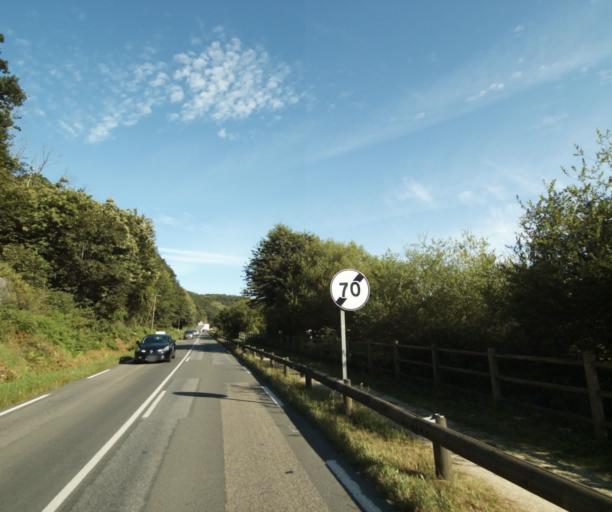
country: FR
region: Pays de la Loire
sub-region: Departement de la Mayenne
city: Laval
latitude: 48.0366
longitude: -0.7595
